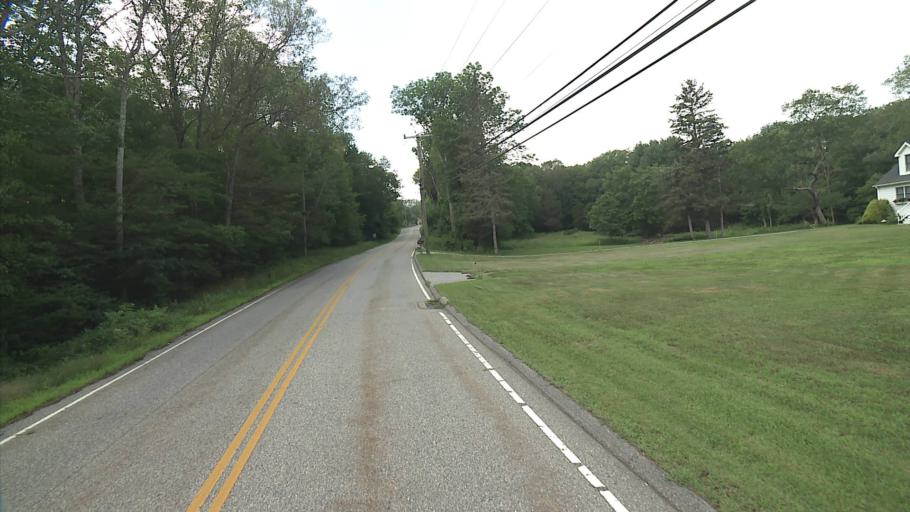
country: US
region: Connecticut
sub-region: New London County
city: Lisbon
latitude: 41.6143
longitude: -72.0473
